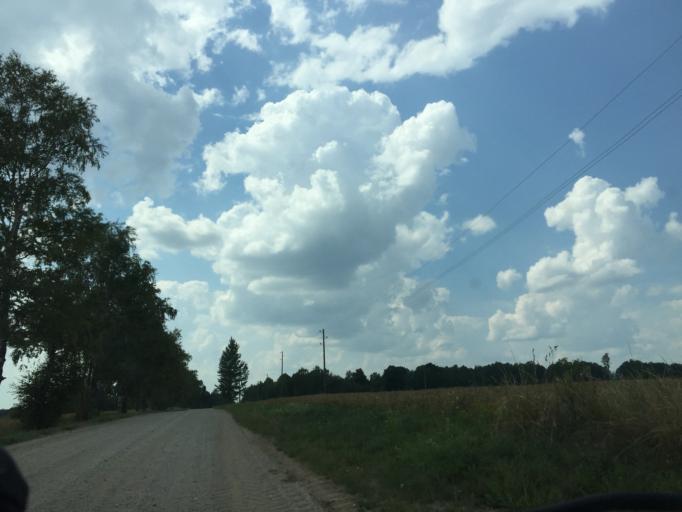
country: LT
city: Zagare
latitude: 56.3387
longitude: 23.1053
